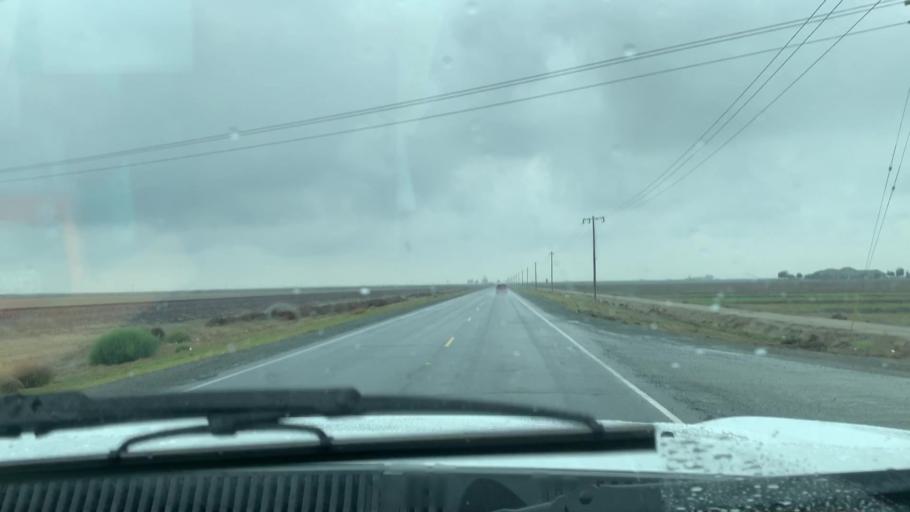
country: US
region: California
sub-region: Tulare County
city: Alpaugh
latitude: 35.9638
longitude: -119.4582
